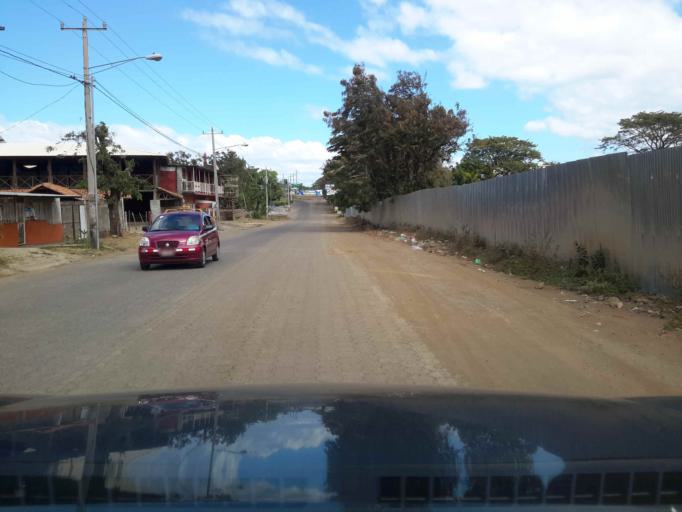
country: NI
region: Managua
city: Managua
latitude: 12.1343
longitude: -86.2717
